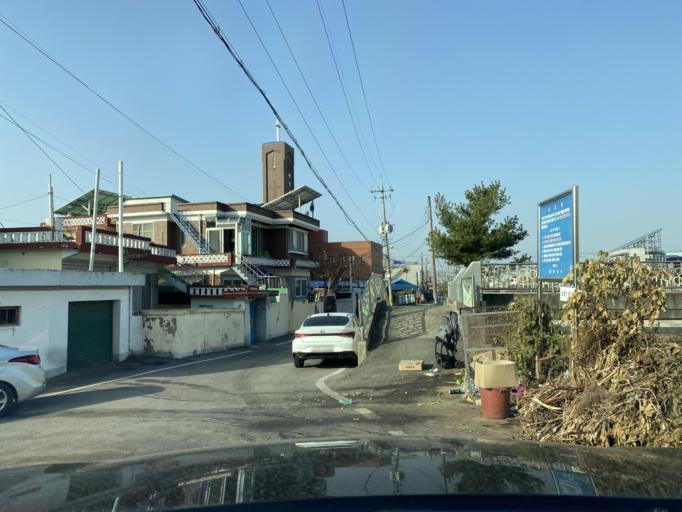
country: KR
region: Chungcheongnam-do
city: Yesan
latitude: 36.6811
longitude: 126.8313
